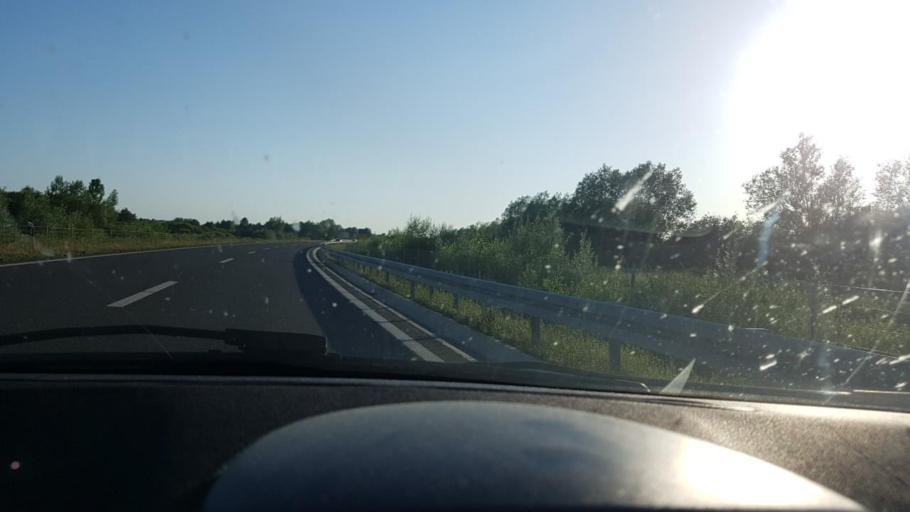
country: HR
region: Krapinsko-Zagorska
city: Zabok
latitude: 46.0150
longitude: 15.9505
